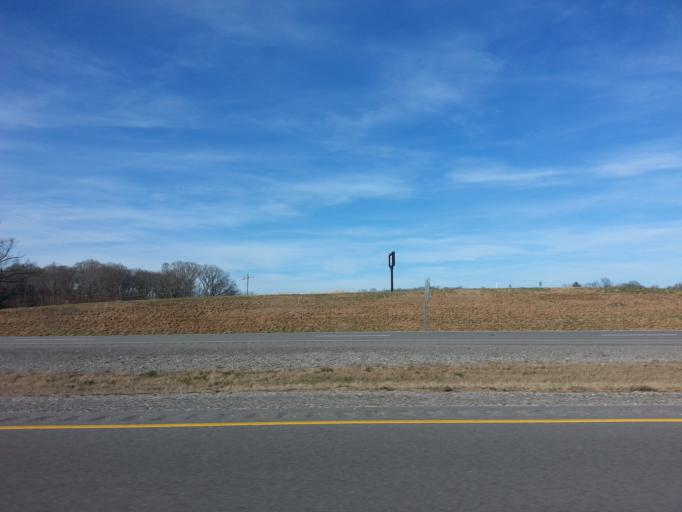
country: US
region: Tennessee
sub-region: Warren County
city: McMinnville
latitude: 35.7306
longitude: -85.9154
